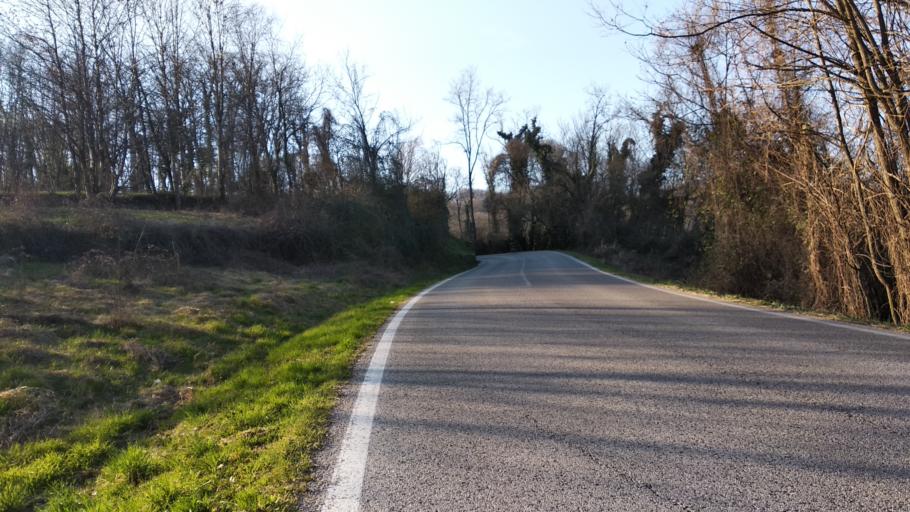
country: IT
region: Veneto
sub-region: Provincia di Vicenza
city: Monte di Malo
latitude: 45.6683
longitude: 11.3686
